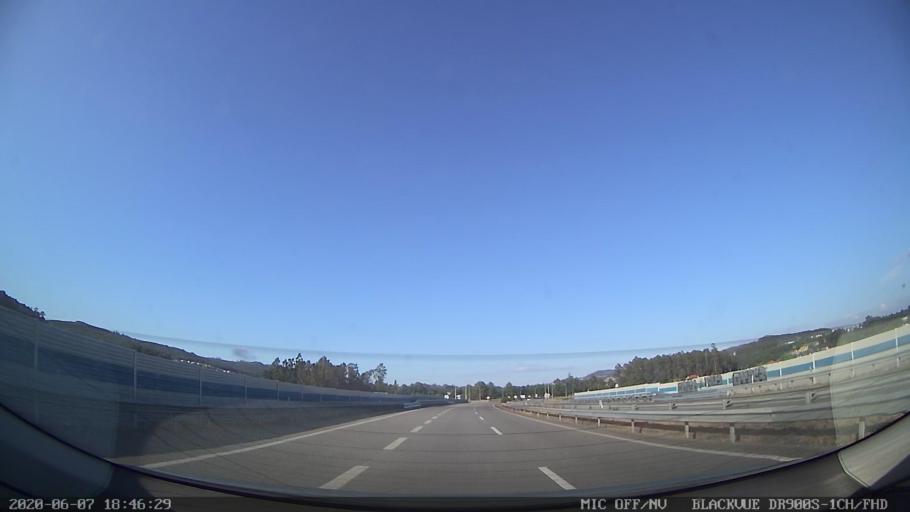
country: PT
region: Braga
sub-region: Vila Nova de Famalicao
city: Vila Nova de Famalicao
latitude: 41.4003
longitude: -8.4651
